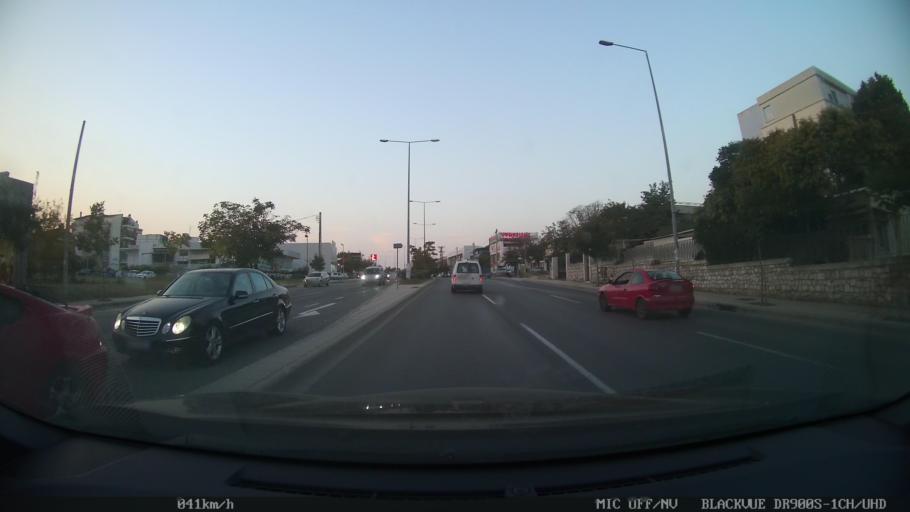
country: GR
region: Central Macedonia
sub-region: Nomos Thessalonikis
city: Kalamaria
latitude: 40.5774
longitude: 22.9694
